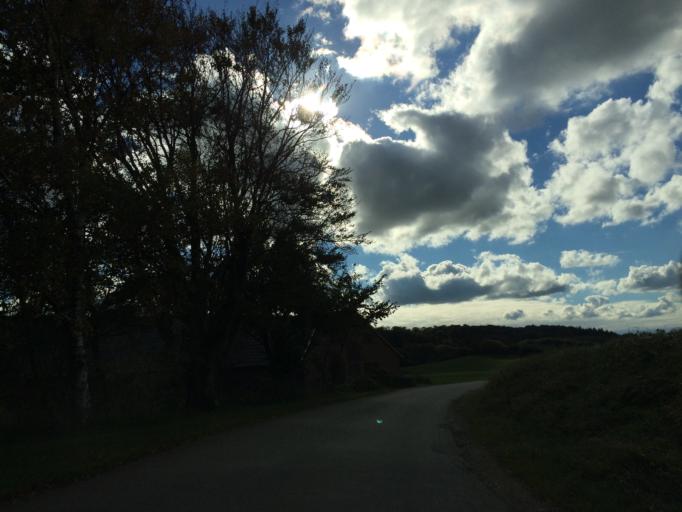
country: DK
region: Central Jutland
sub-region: Skanderborg Kommune
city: Ry
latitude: 56.1656
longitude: 9.7743
